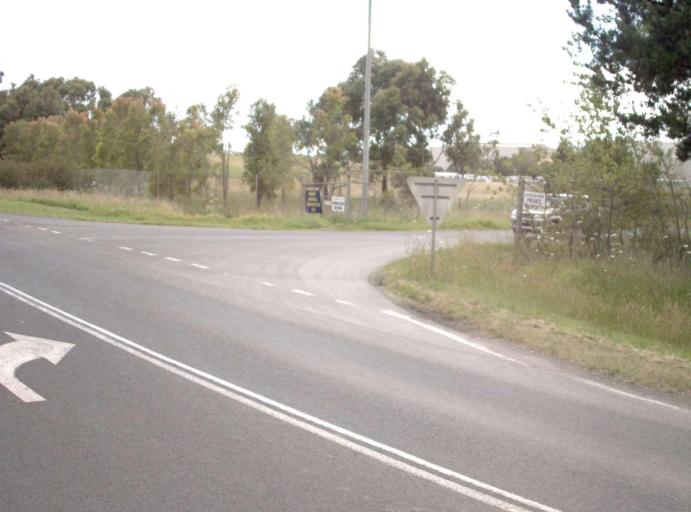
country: AU
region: Victoria
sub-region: Latrobe
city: Morwell
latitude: -38.1797
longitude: 146.4412
